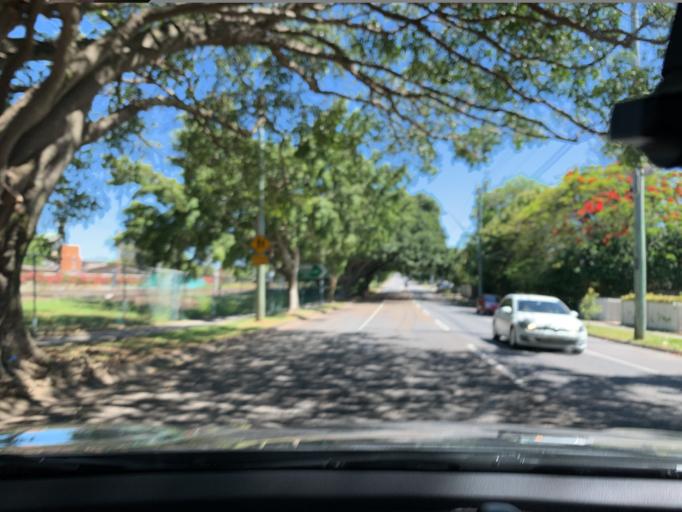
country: AU
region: Queensland
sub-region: Brisbane
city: Ascot
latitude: -27.4268
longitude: 153.0628
